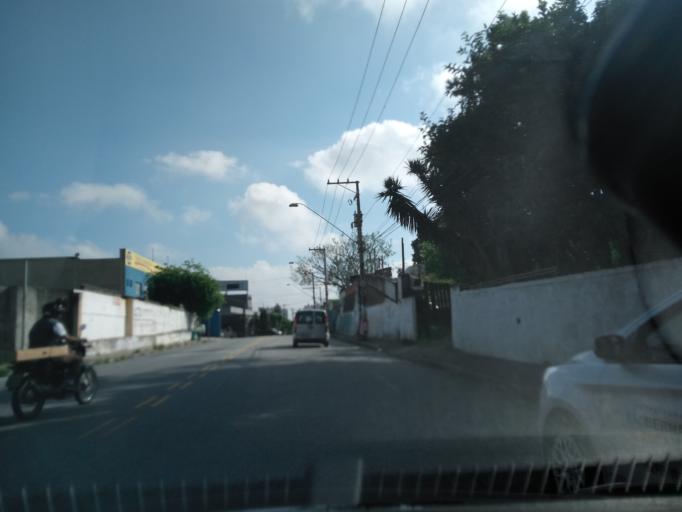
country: BR
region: Sao Paulo
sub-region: Sao Bernardo Do Campo
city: Sao Bernardo do Campo
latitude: -23.7250
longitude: -46.5553
